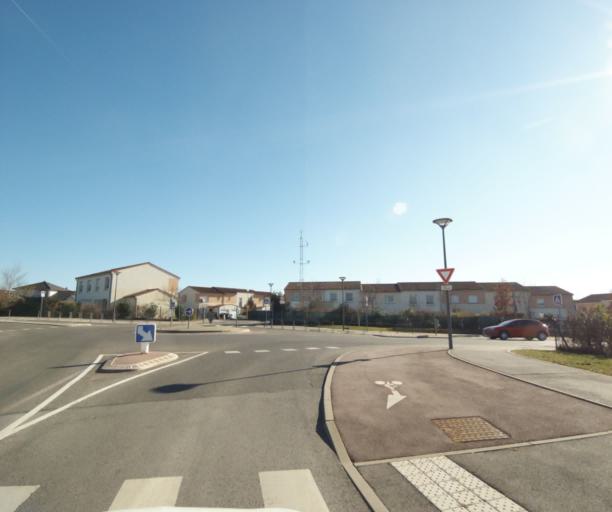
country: FR
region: Lorraine
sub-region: Departement de Meurthe-et-Moselle
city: Tomblaine
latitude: 48.6759
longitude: 6.2295
